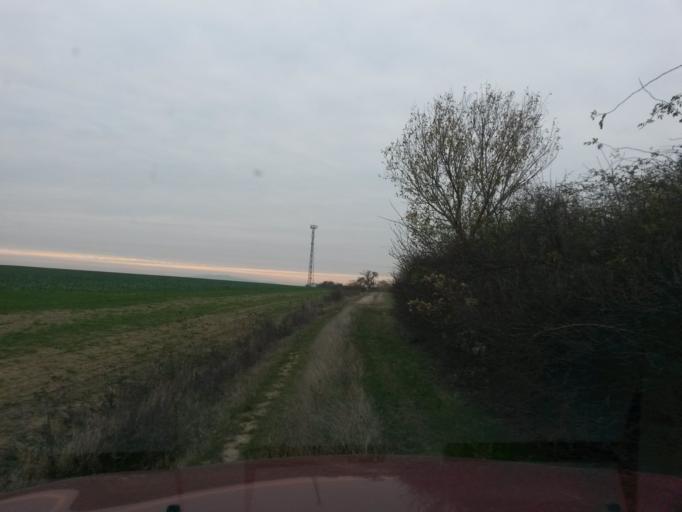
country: SK
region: Kosicky
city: Secovce
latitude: 48.6419
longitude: 21.6268
